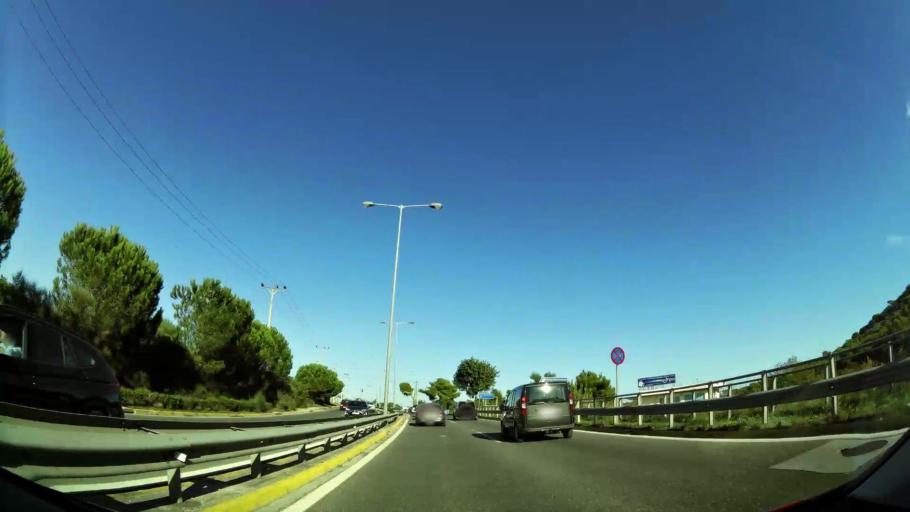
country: GR
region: Attica
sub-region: Nomarchia Anatolikis Attikis
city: Pikermi
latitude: 38.0071
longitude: 23.9585
